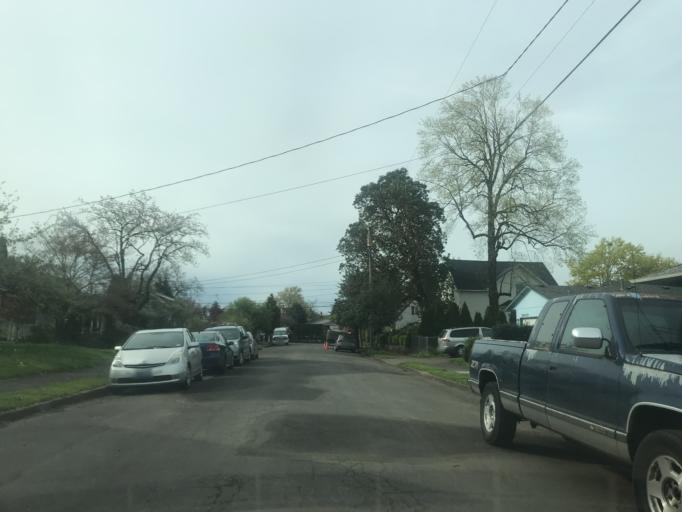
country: US
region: Oregon
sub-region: Multnomah County
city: Lents
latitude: 45.4949
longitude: -122.5932
